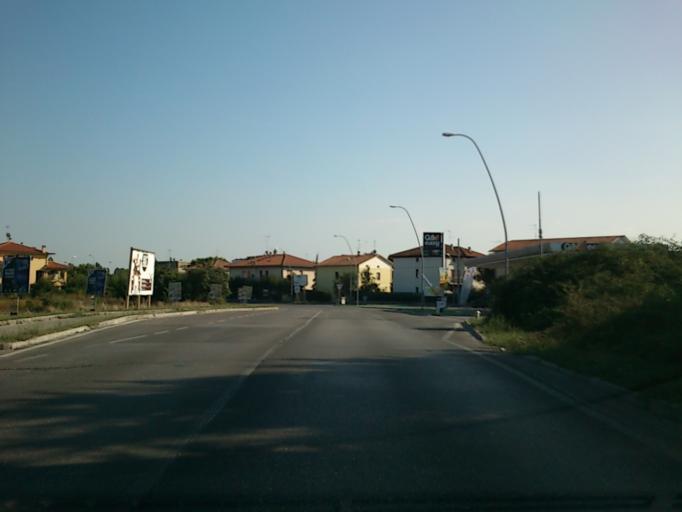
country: IT
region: The Marches
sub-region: Provincia di Pesaro e Urbino
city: Fano
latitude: 43.8337
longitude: 13.0118
